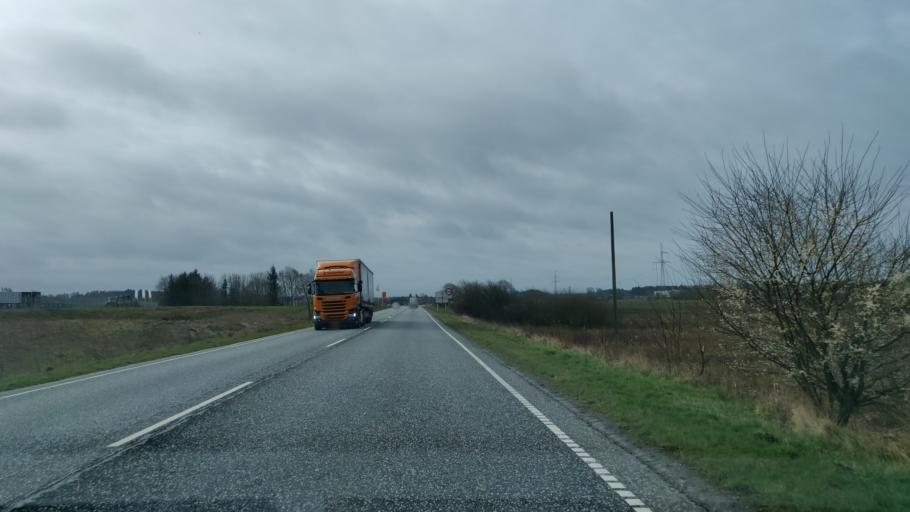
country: DK
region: North Denmark
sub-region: Vesthimmerland Kommune
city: Alestrup
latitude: 56.6685
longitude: 9.5219
